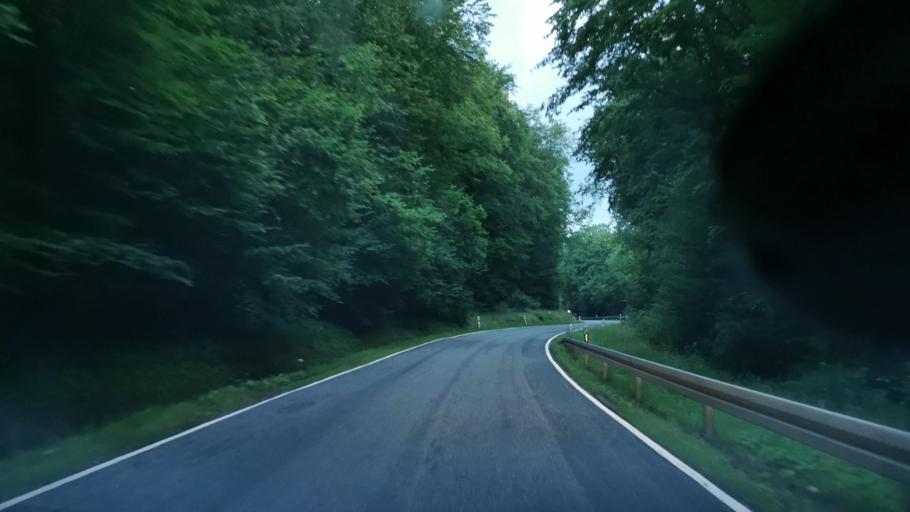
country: DE
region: Rheinland-Pfalz
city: Breitenbach
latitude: 49.4074
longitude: 7.2532
